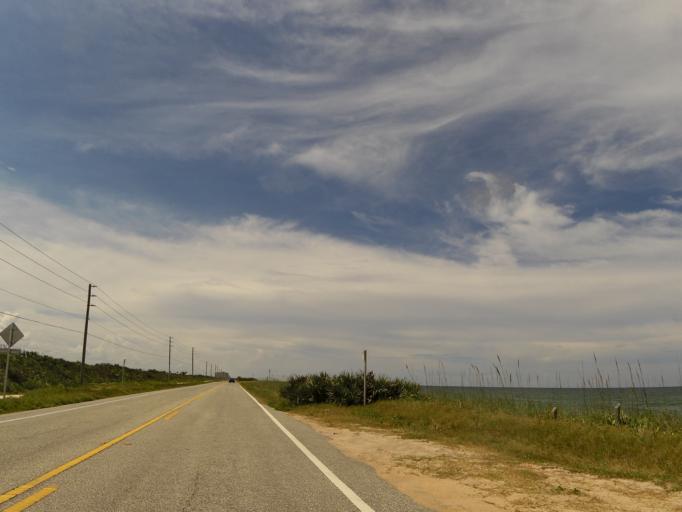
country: US
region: Florida
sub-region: Volusia County
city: Ormond-by-the-Sea
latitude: 29.4114
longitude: -81.0954
